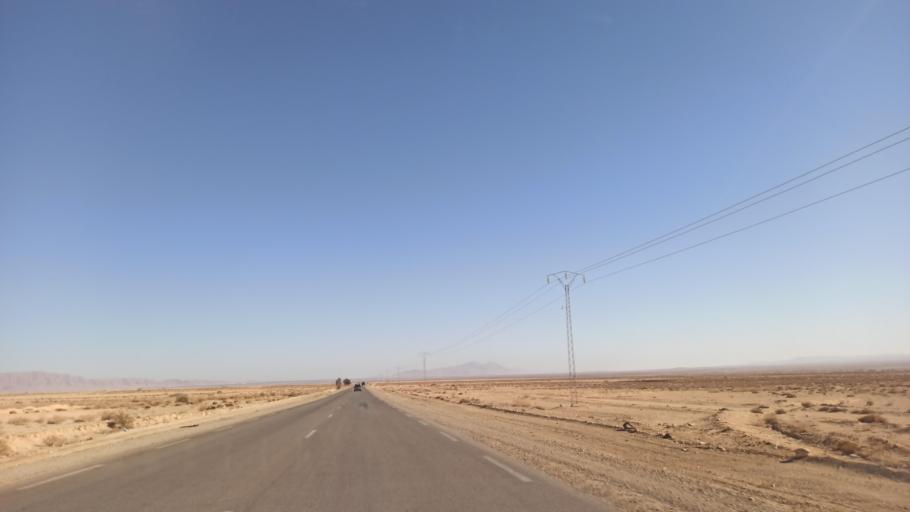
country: TN
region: Gafsa
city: Al Metlaoui
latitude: 34.3198
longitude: 8.5161
